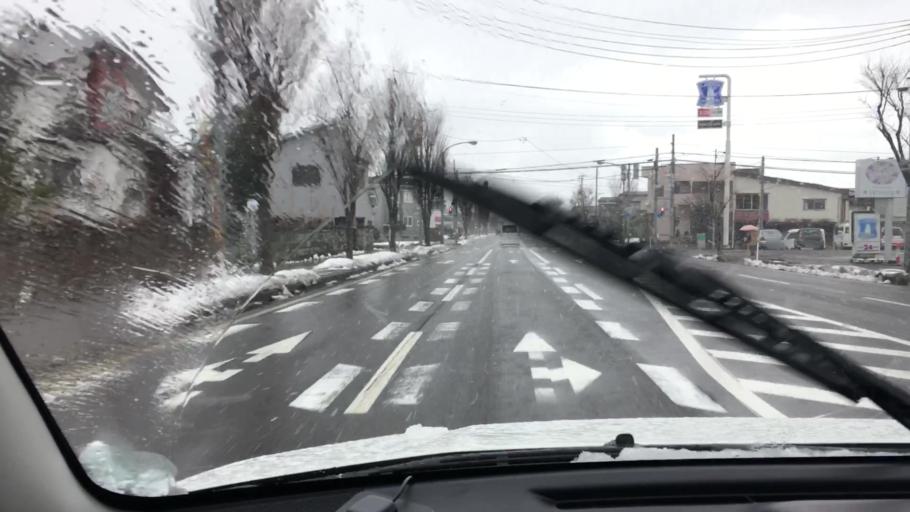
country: JP
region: Niigata
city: Joetsu
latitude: 37.1169
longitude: 138.2329
